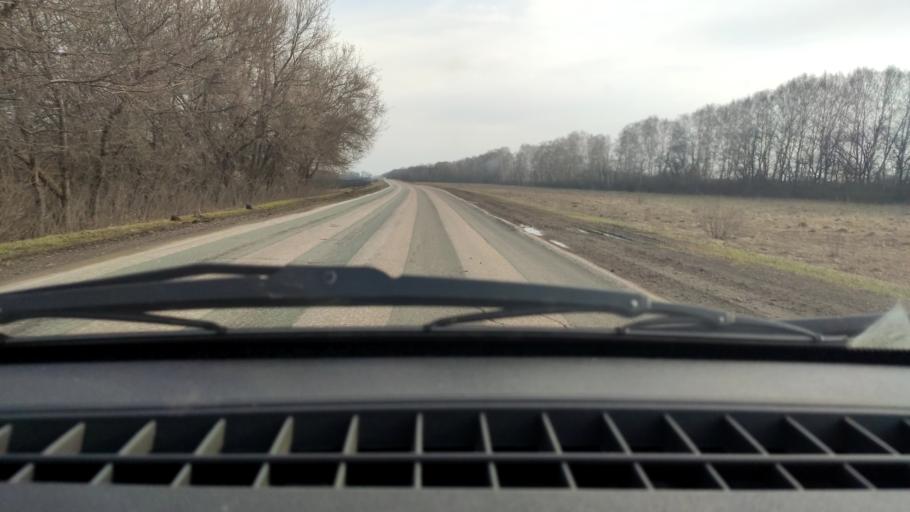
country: RU
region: Bashkortostan
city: Chishmy
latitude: 54.4526
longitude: 55.2493
